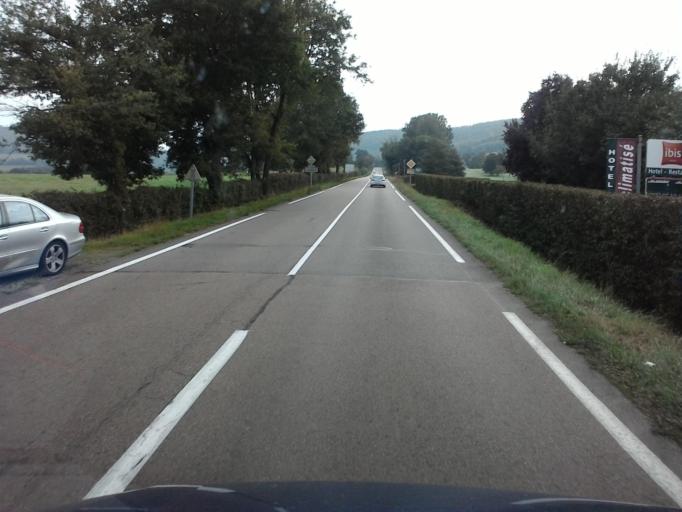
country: FR
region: Bourgogne
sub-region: Departement de Saone-et-Loire
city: Autun
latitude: 46.9541
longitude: 4.3216
